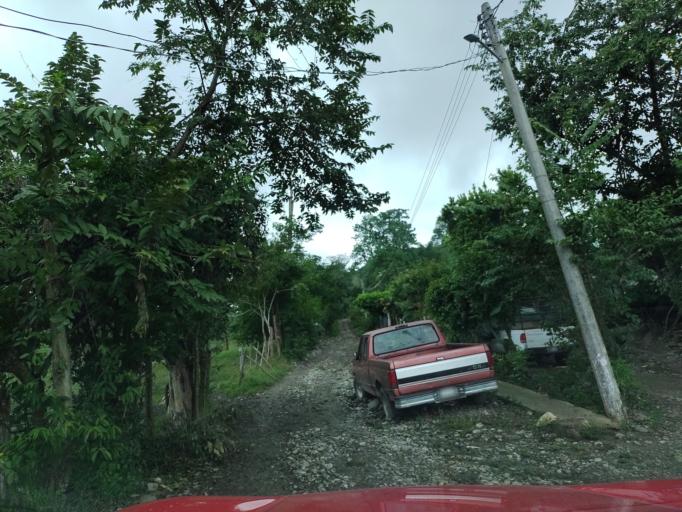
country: MX
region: Puebla
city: Espinal
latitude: 20.2614
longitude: -97.3750
